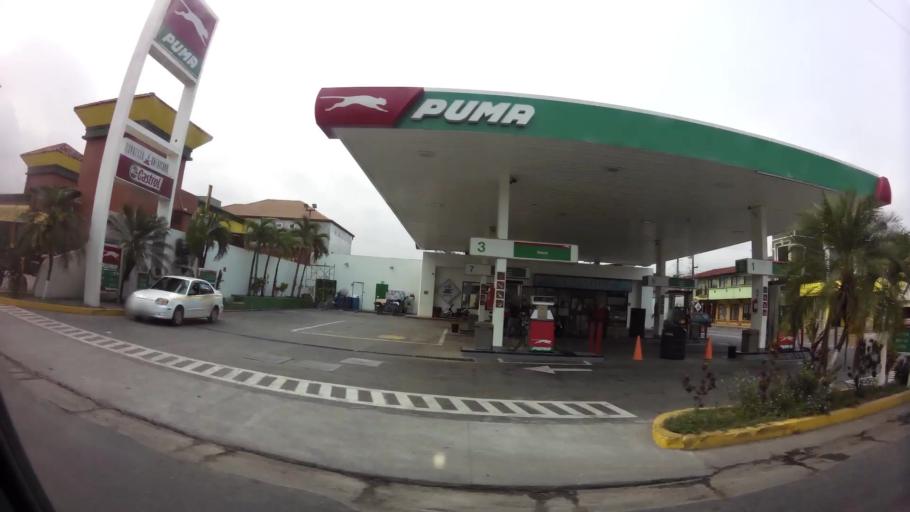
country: HN
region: Yoro
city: El Progreso
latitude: 15.4036
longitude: -87.8122
